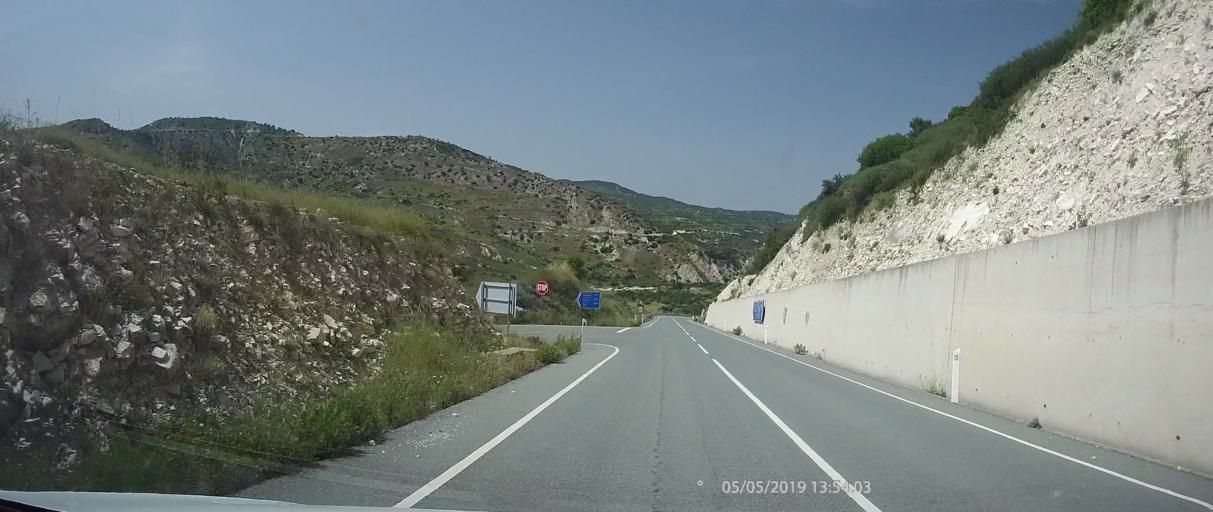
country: CY
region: Limassol
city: Pachna
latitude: 34.8174
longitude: 32.7213
